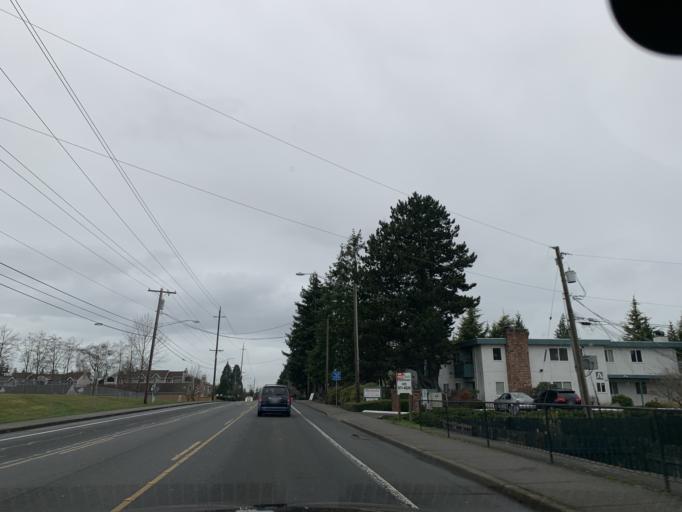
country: US
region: Washington
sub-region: Snohomish County
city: Mukilteo
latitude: 47.9219
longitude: -122.2509
